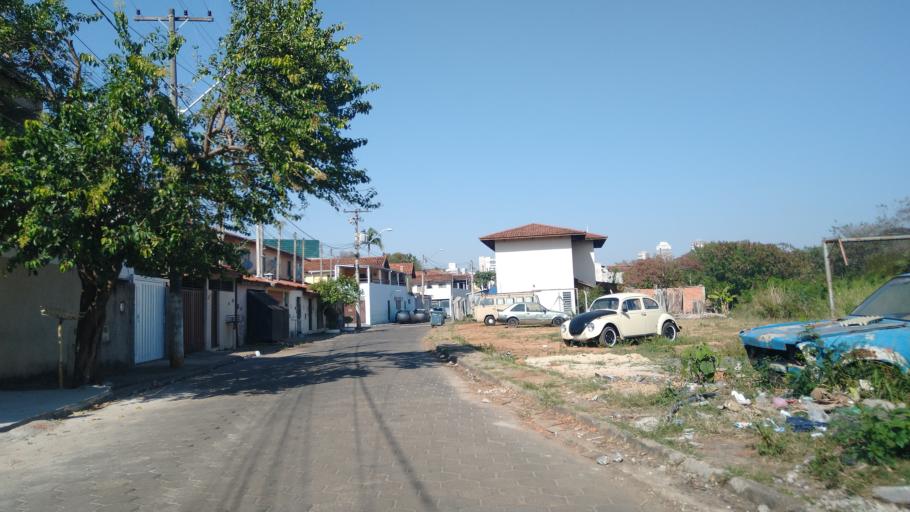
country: BR
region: Sao Paulo
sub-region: Campinas
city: Campinas
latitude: -22.8817
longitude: -47.0389
